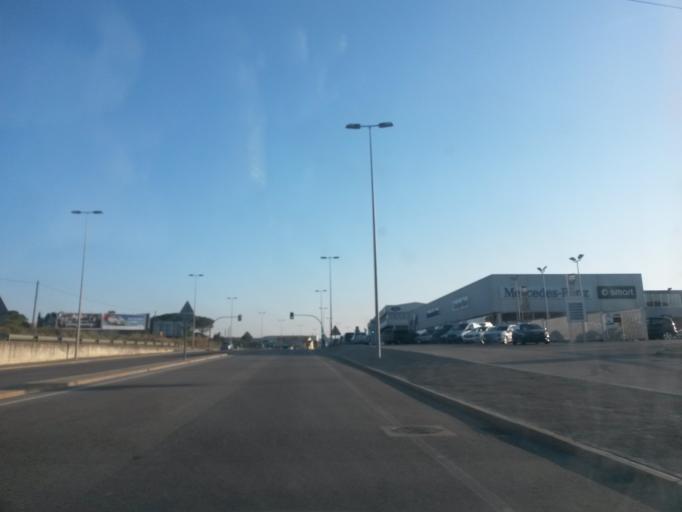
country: ES
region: Catalonia
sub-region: Provincia de Girona
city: Fornells de la Selva
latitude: 41.9396
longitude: 2.8020
